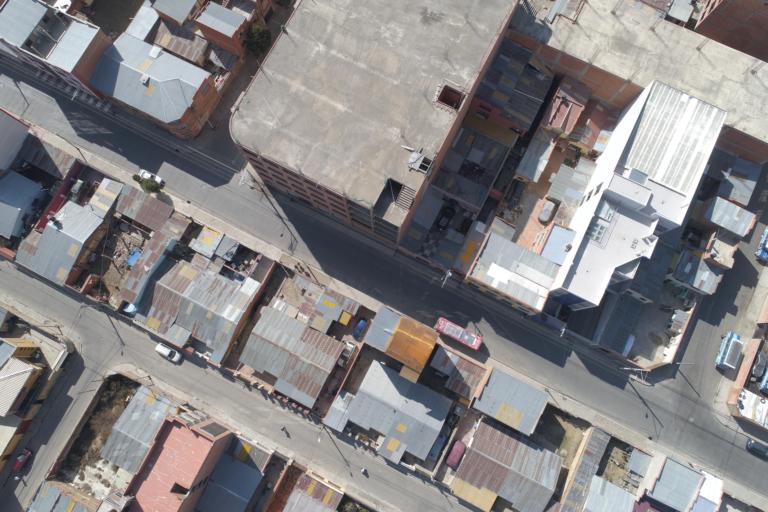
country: BO
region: La Paz
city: La Paz
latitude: -16.5287
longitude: -68.1493
